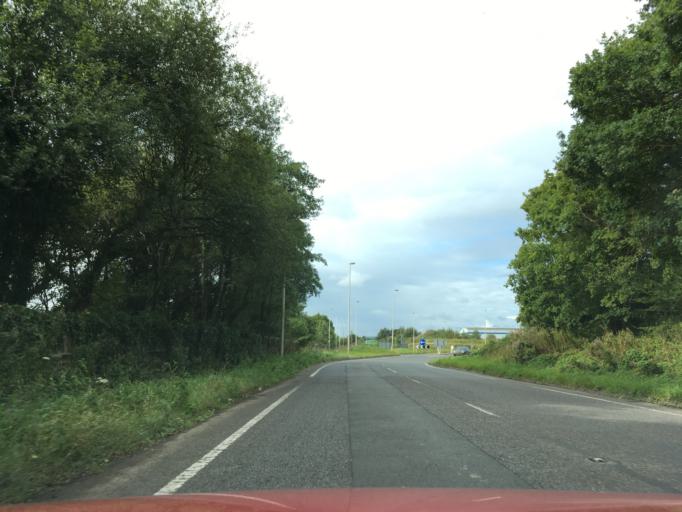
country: GB
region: England
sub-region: Gloucestershire
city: Lydney
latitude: 51.7186
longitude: -2.5174
